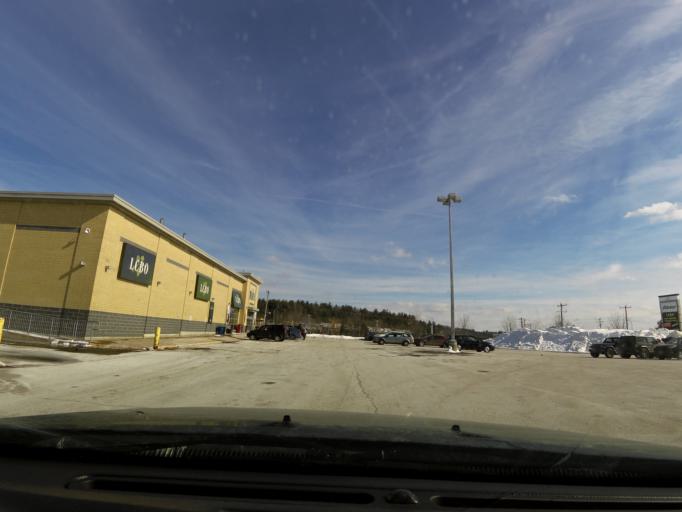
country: CA
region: Ontario
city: Gravenhurst
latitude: 44.9081
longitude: -79.3705
